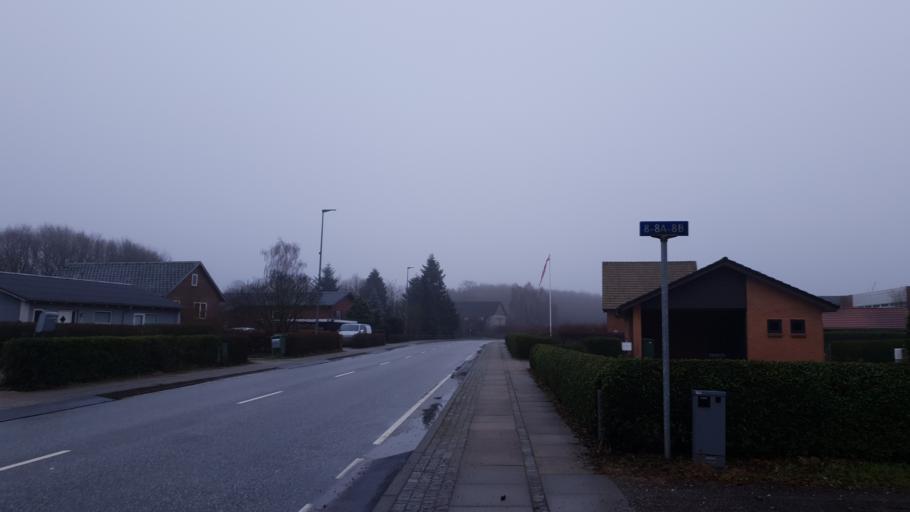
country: DK
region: Central Jutland
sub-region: Hedensted Kommune
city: Hedensted
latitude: 55.7974
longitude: 9.6988
